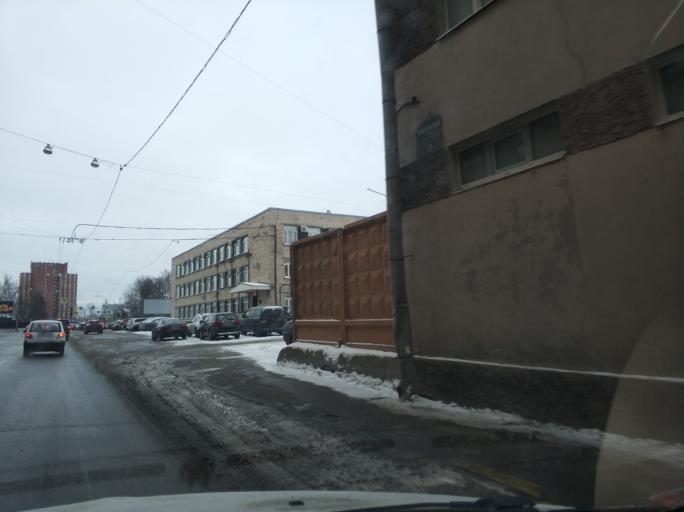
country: RU
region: St.-Petersburg
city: Centralniy
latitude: 59.9179
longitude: 30.3742
